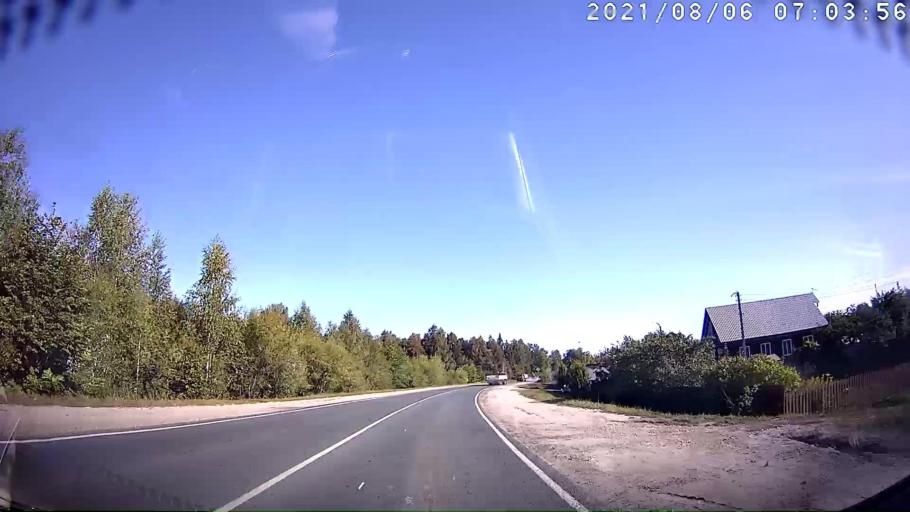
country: RU
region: Mariy-El
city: Yoshkar-Ola
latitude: 56.5433
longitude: 47.9815
